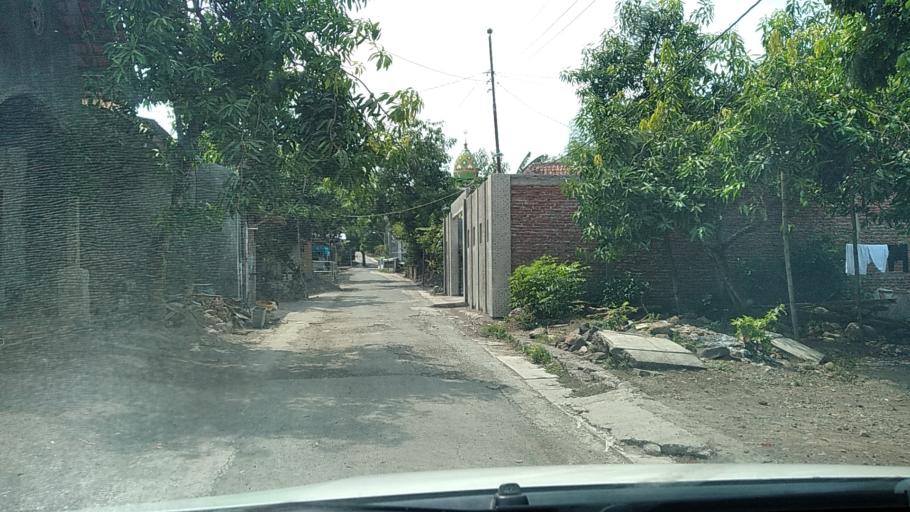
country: ID
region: Central Java
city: Mranggen
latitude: -7.0625
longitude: 110.4794
